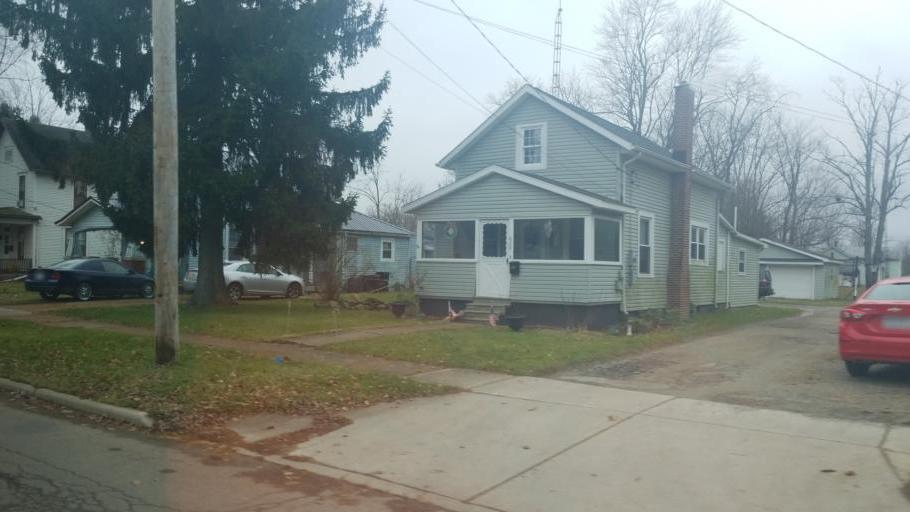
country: US
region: Ohio
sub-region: Crawford County
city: Galion
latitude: 40.7256
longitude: -82.7931
